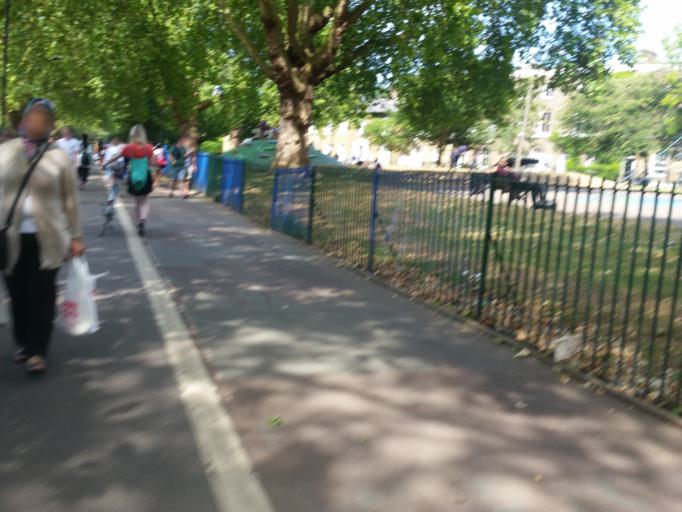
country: GB
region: England
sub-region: Greater London
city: Bethnal Green
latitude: 51.5390
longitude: -0.0600
